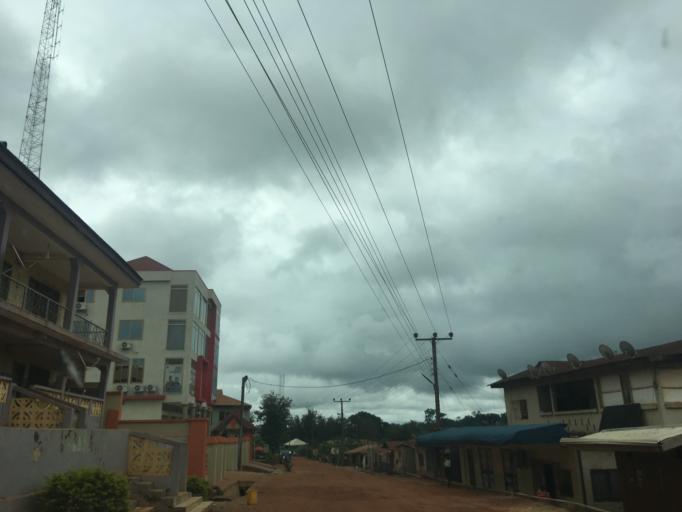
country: GH
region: Western
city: Wassa-Akropong
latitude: 5.8111
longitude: -2.4348
